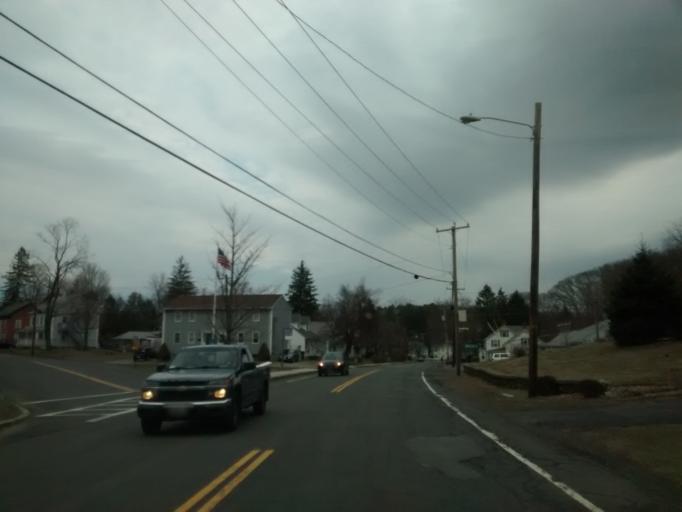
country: US
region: Massachusetts
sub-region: Worcester County
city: Grafton
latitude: 42.1769
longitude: -71.7093
